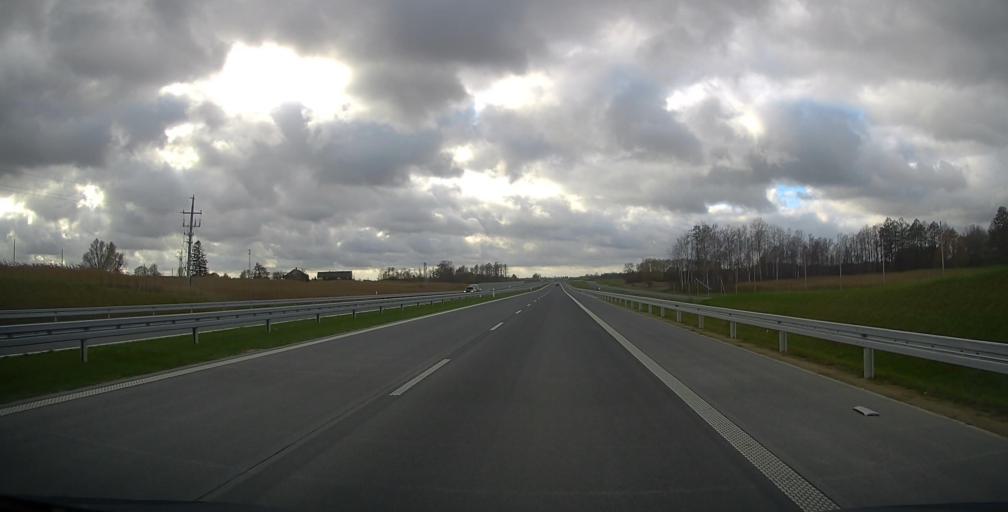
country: PL
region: Podlasie
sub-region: Powiat suwalski
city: Raczki
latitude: 53.9165
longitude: 22.7338
